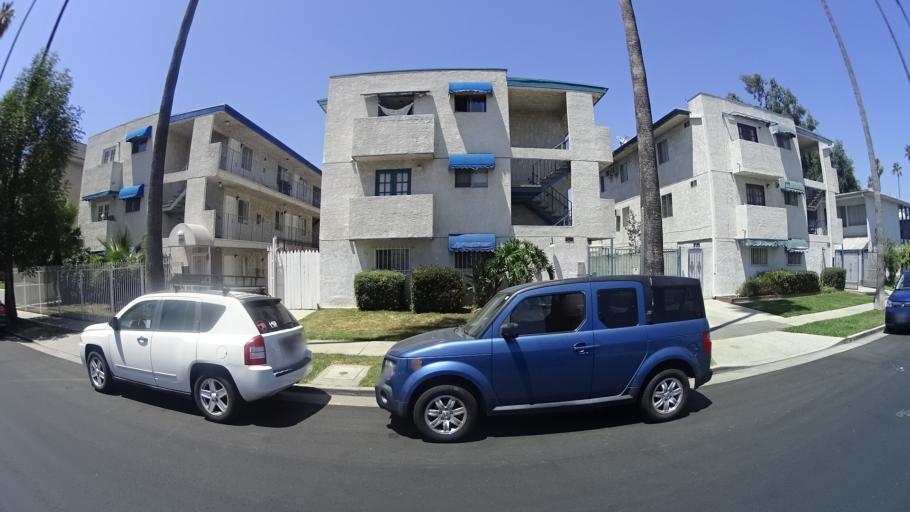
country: US
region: California
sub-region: Los Angeles County
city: Van Nuys
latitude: 34.1897
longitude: -118.4454
